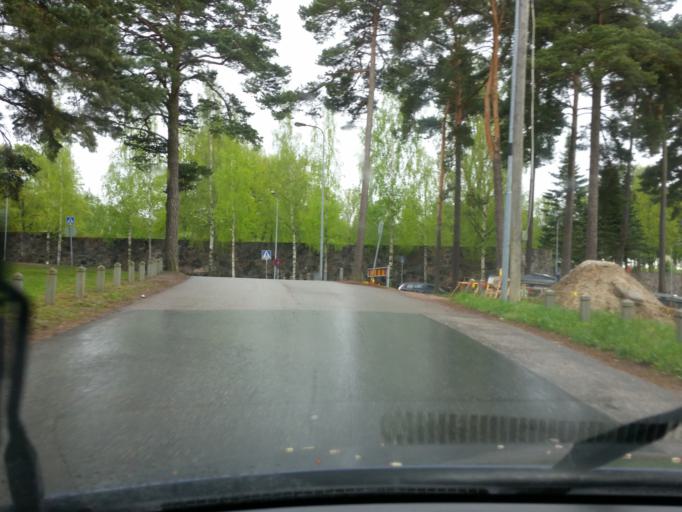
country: FI
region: Uusimaa
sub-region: Helsinki
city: Helsinki
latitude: 60.1738
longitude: 24.9085
